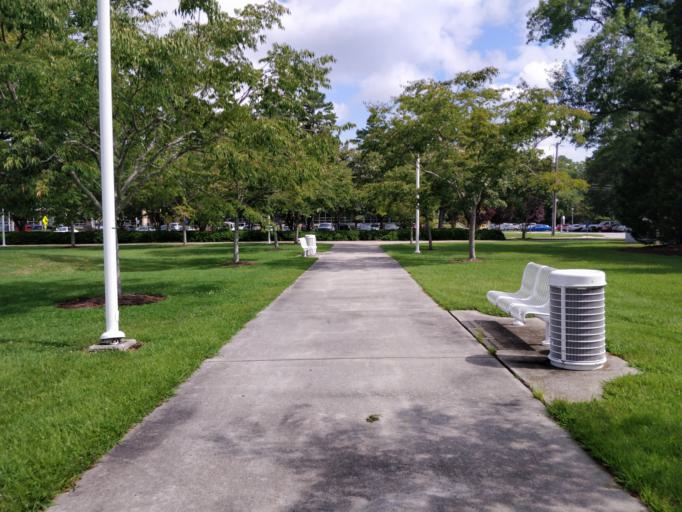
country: US
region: Virginia
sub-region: City of Chesapeake
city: Chesapeake
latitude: 36.7171
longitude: -76.2490
